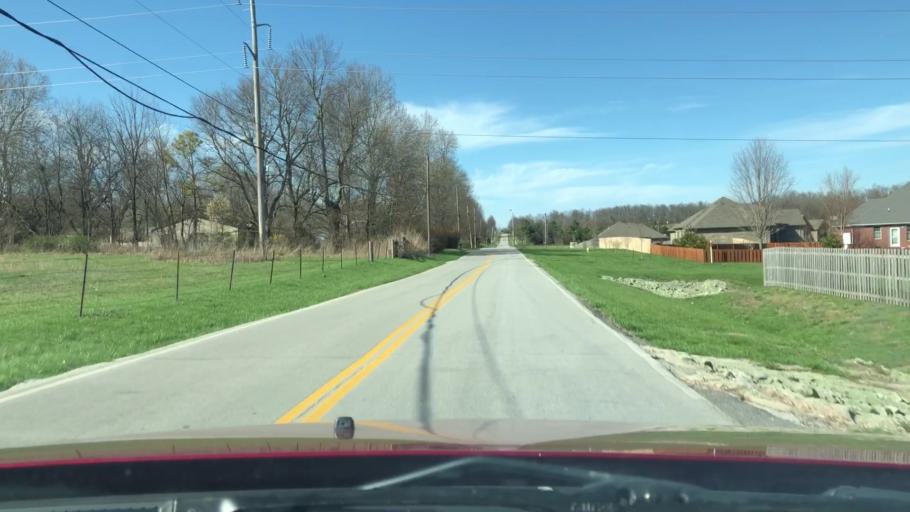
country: US
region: Missouri
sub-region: Greene County
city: Strafford
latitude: 37.2298
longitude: -93.1884
